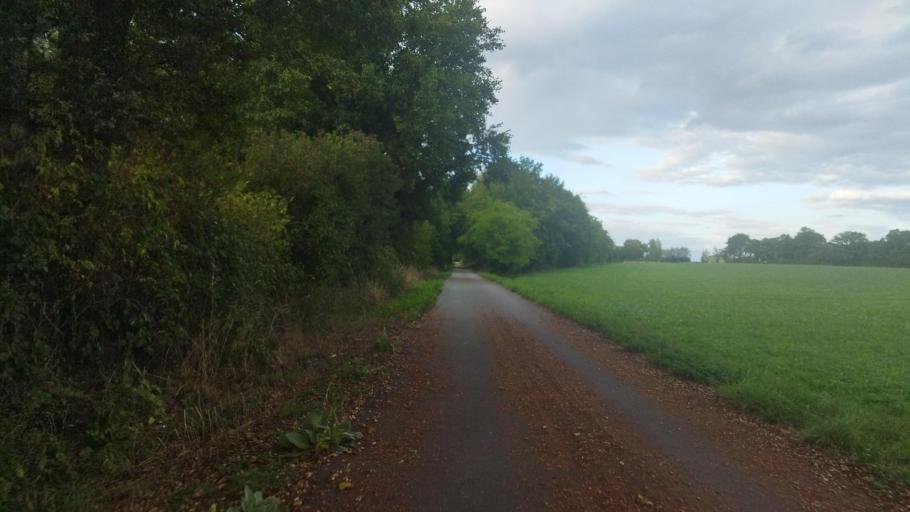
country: DE
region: North Rhine-Westphalia
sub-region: Regierungsbezirk Munster
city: Billerbeck
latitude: 51.9887
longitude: 7.2338
